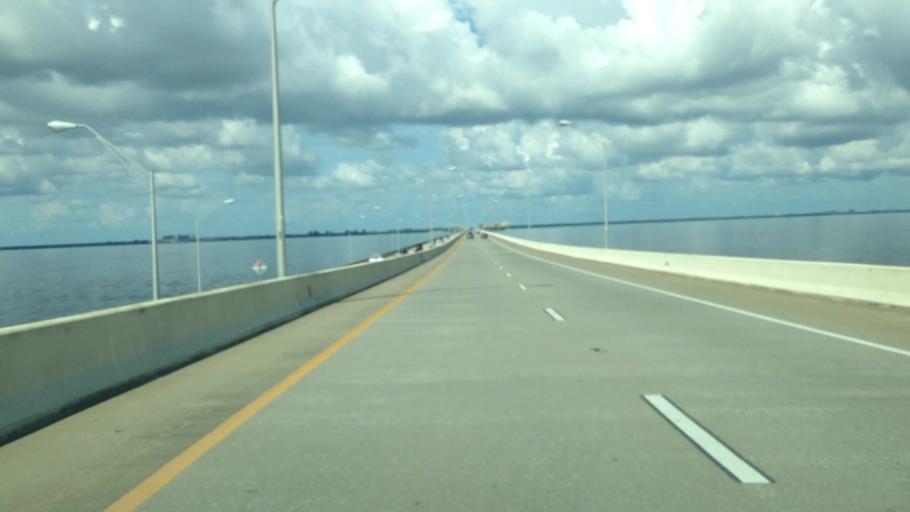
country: US
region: Florida
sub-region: Pinellas County
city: Gandy
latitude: 27.8864
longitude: -82.5561
